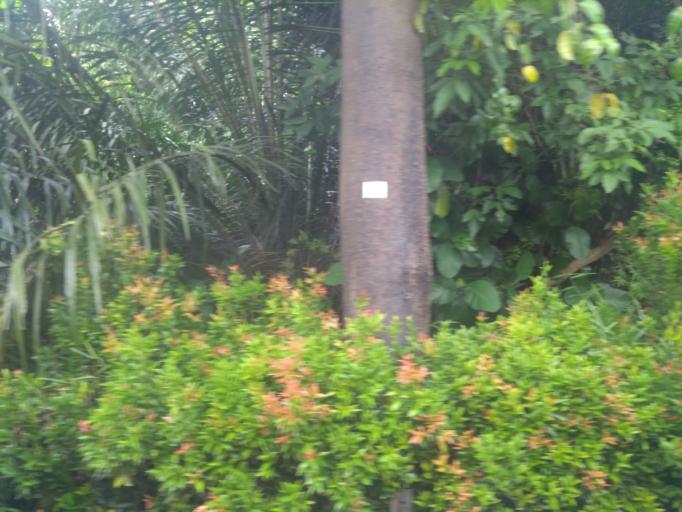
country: MY
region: Johor
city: Johor Bahru
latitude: 1.4902
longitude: 103.7360
